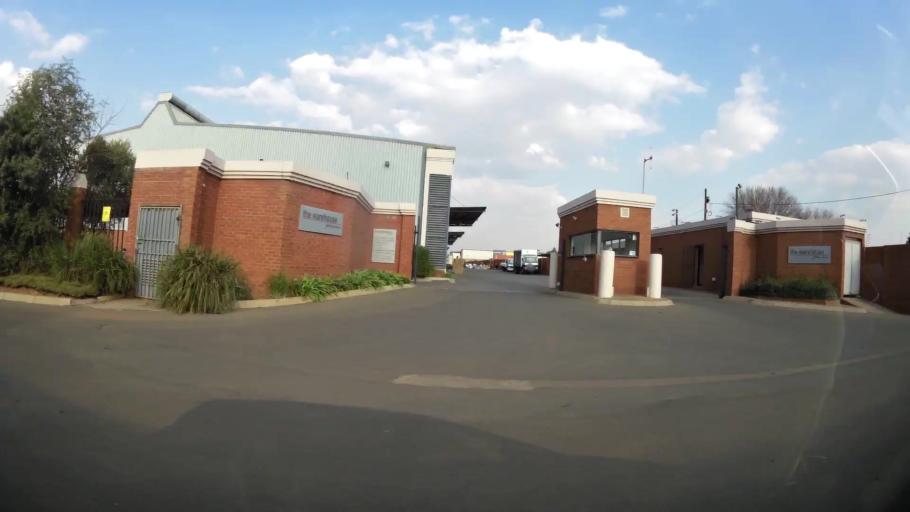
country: ZA
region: Gauteng
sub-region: Ekurhuleni Metropolitan Municipality
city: Benoni
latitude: -26.1099
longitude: 28.2705
